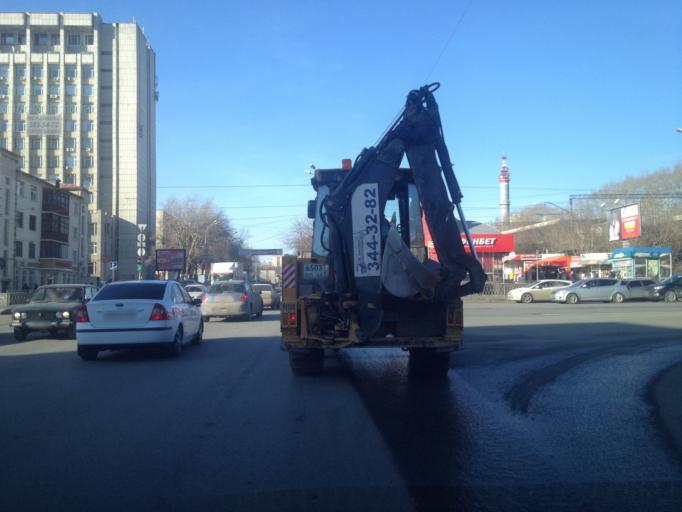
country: RU
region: Sverdlovsk
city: Yekaterinburg
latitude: 56.8413
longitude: 60.6322
